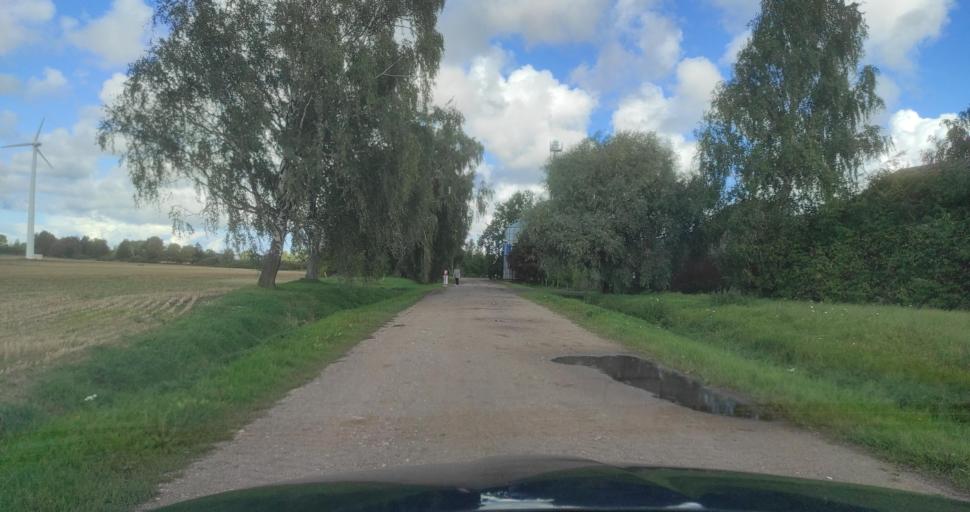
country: LV
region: Ventspils Rajons
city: Piltene
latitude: 57.2674
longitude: 21.5884
